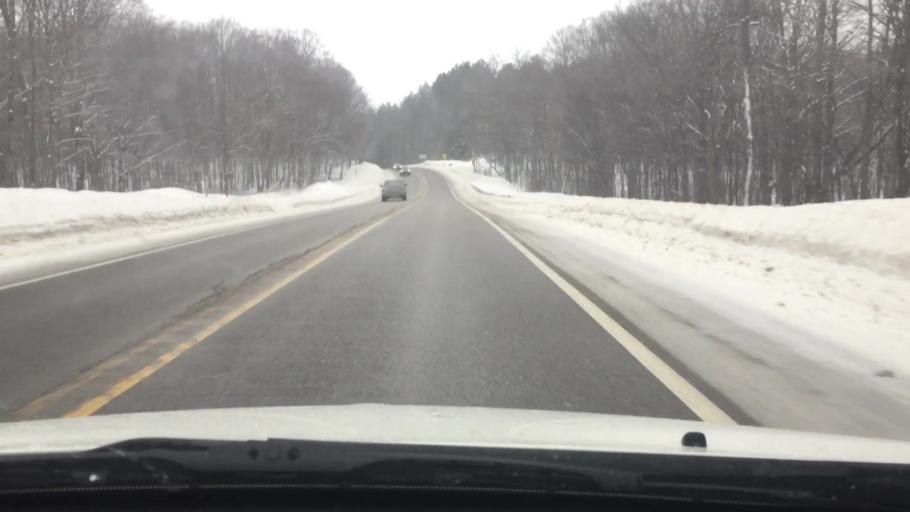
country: US
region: Michigan
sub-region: Otsego County
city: Gaylord
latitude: 45.0612
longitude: -84.7988
